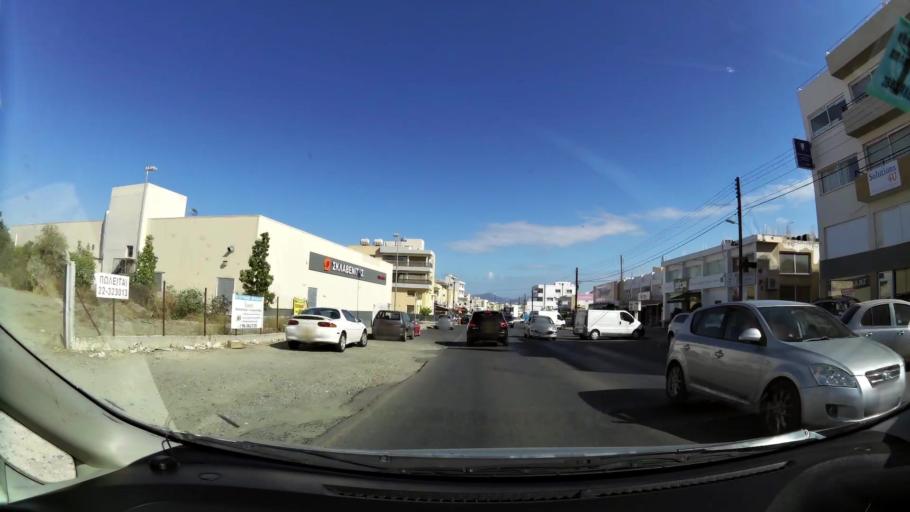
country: CY
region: Lefkosia
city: Nicosia
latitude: 35.1310
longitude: 33.3387
